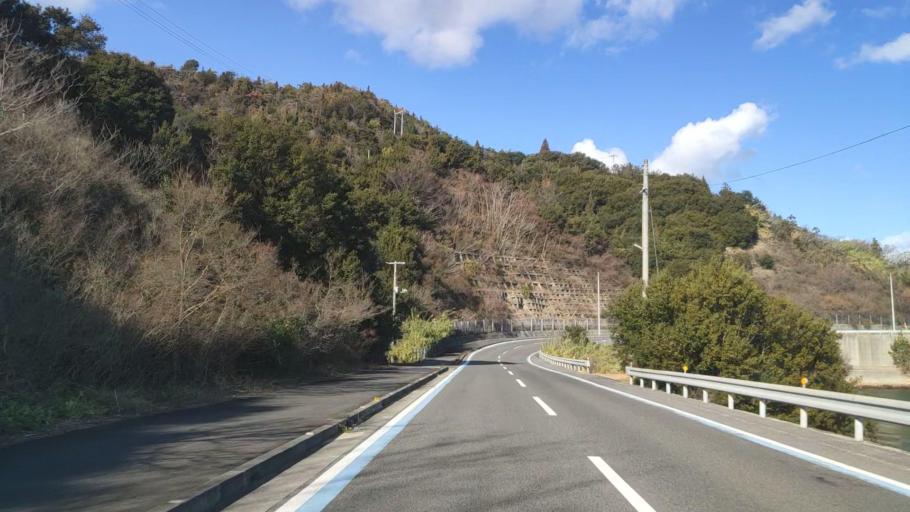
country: JP
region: Hiroshima
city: Innoshima
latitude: 34.2251
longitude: 133.1082
